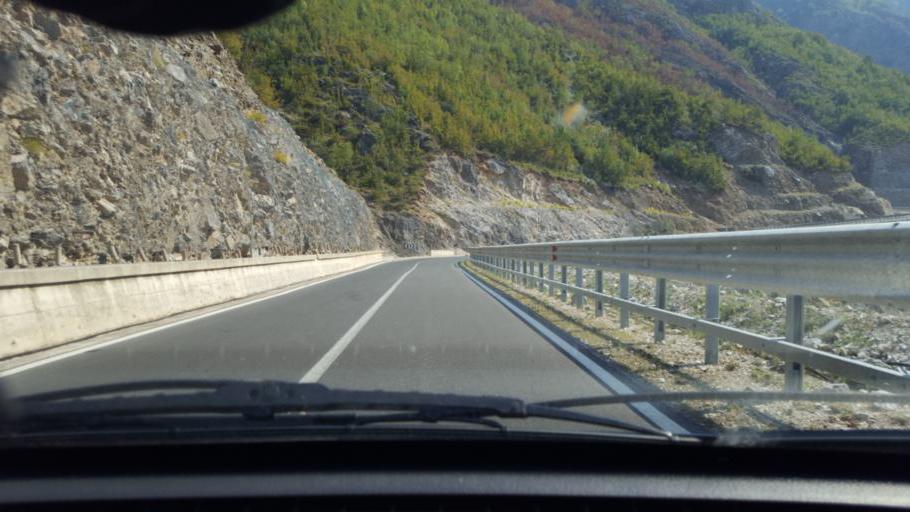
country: AL
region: Shkoder
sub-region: Rrethi i Malesia e Madhe
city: Kastrat
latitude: 42.4162
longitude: 19.5103
